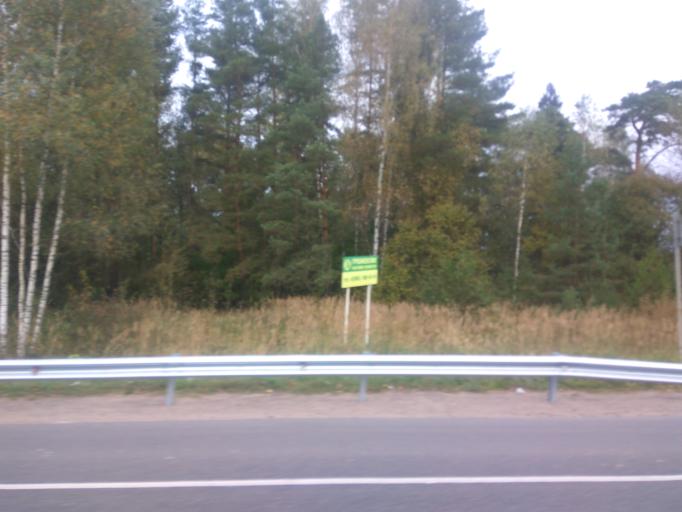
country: RU
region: Moskovskaya
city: Krasnoarmeysk
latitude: 56.0186
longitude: 38.1594
